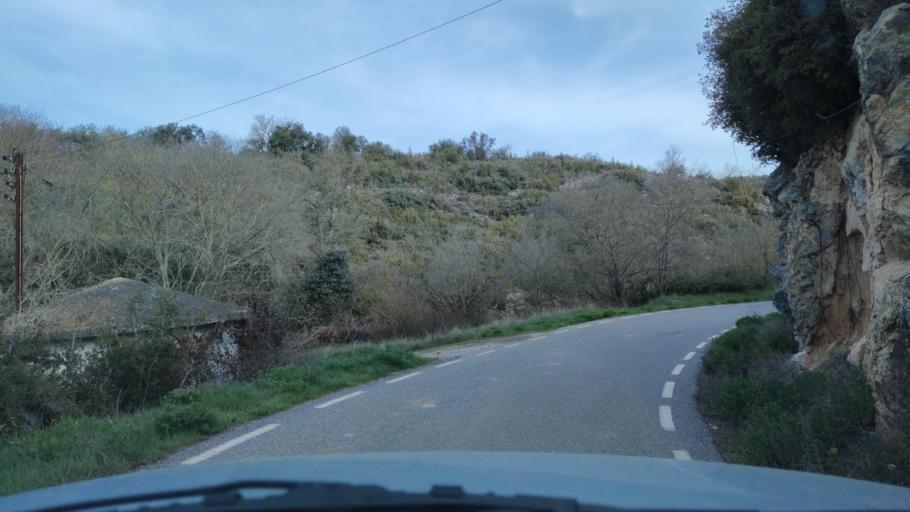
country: ES
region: Catalonia
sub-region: Provincia de Lleida
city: Os de Balaguer
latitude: 41.8849
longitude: 0.7905
